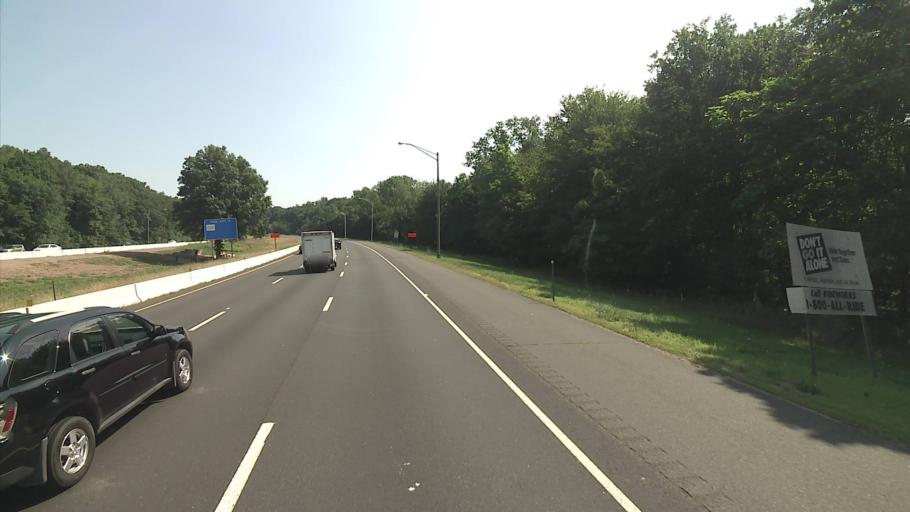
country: US
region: Connecticut
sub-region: New Haven County
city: North Haven
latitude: 41.4032
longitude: -72.8368
